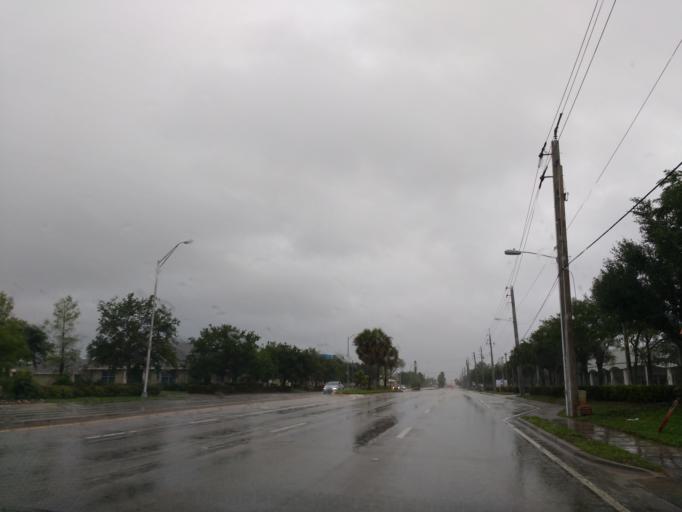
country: US
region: Florida
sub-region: Collier County
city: Naples
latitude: 26.1305
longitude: -81.7663
